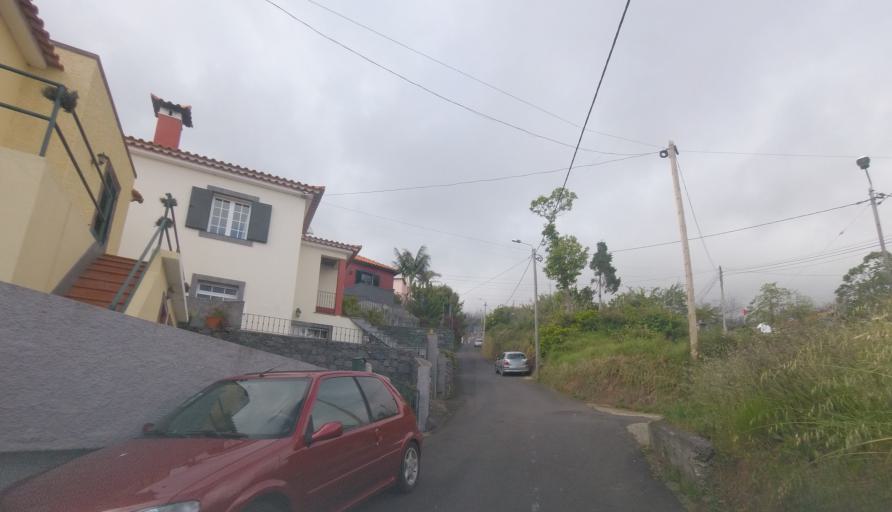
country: PT
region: Madeira
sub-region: Funchal
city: Nossa Senhora do Monte
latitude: 32.6798
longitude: -16.9106
